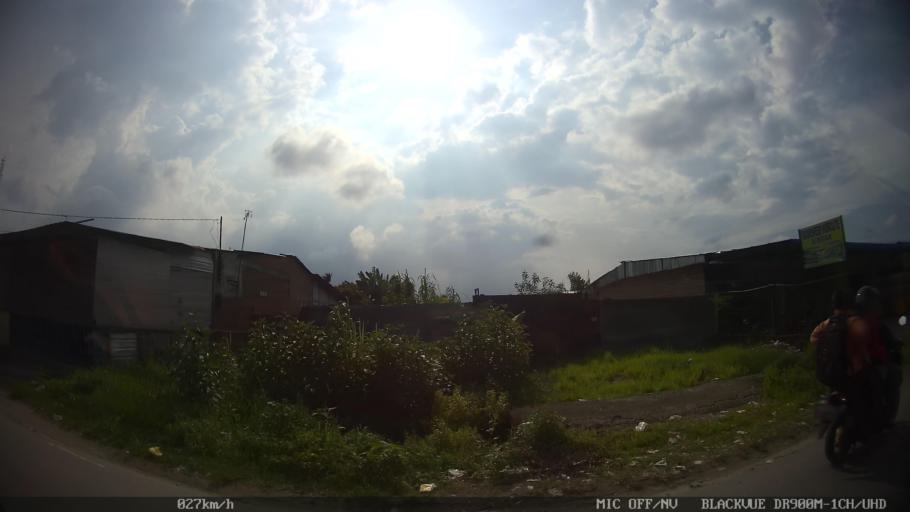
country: ID
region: North Sumatra
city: Medan
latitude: 3.5742
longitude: 98.7566
